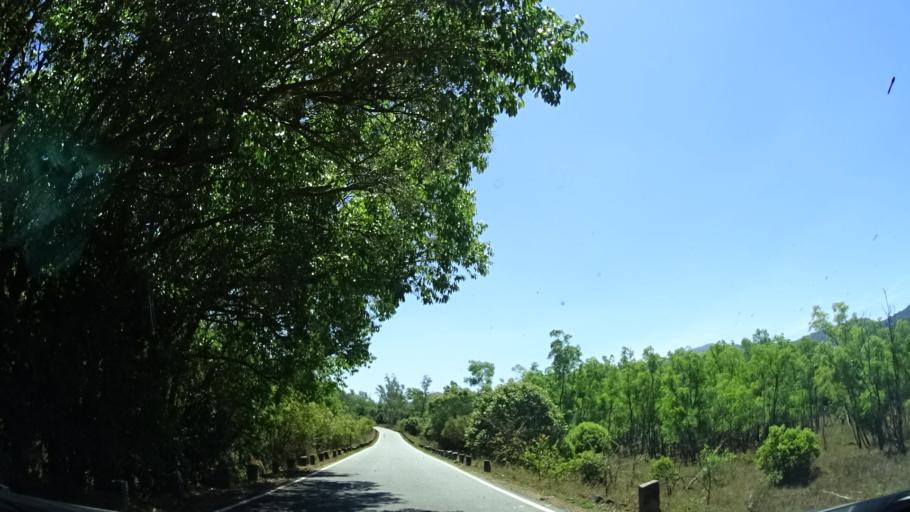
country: IN
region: Karnataka
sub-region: Udupi
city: Karkal
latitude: 13.2109
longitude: 75.1880
